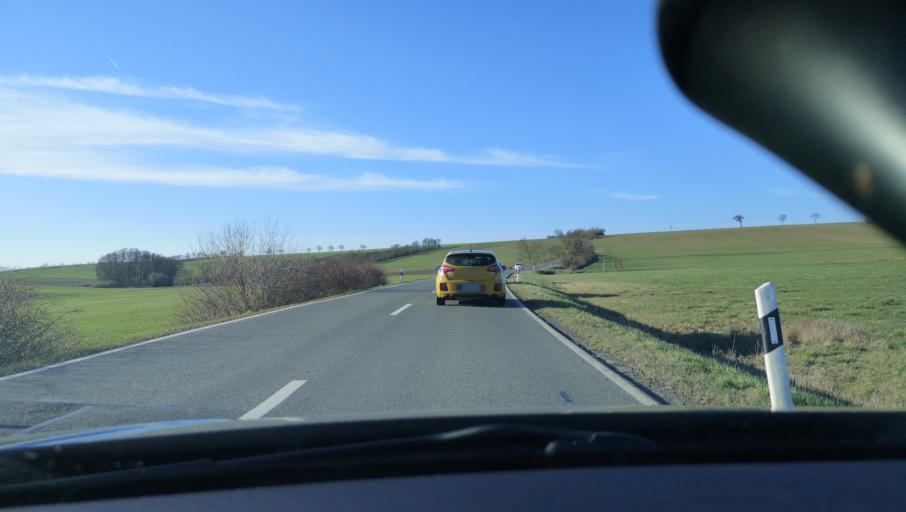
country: DE
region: Bavaria
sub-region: Upper Franconia
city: Sonnefeld
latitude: 50.2429
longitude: 11.1097
